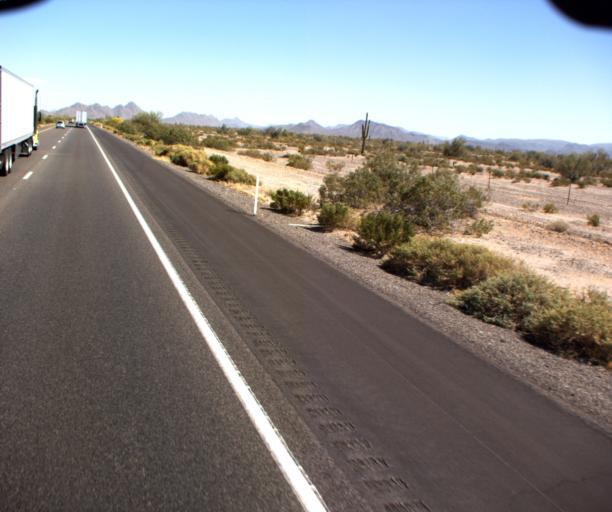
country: US
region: Arizona
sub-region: Maricopa County
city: Gila Bend
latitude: 32.9134
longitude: -112.6178
